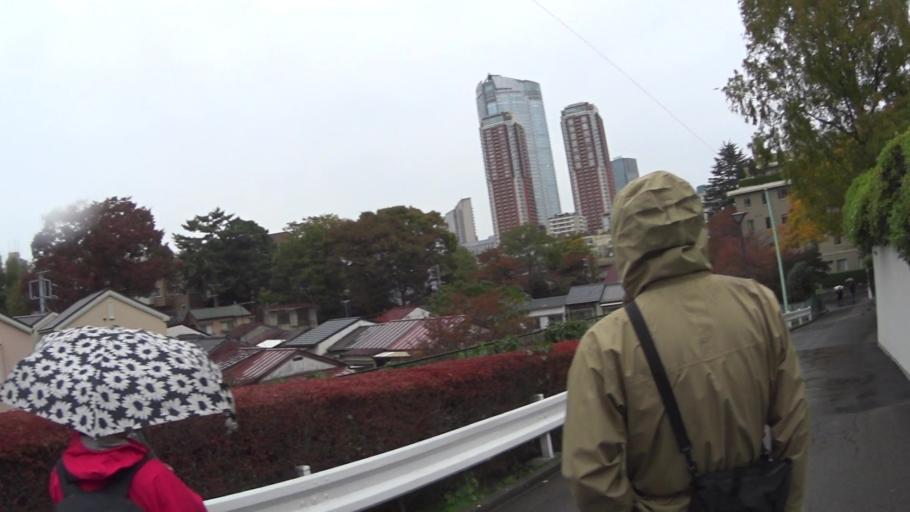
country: JP
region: Tokyo
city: Tokyo
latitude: 35.6543
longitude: 139.7300
